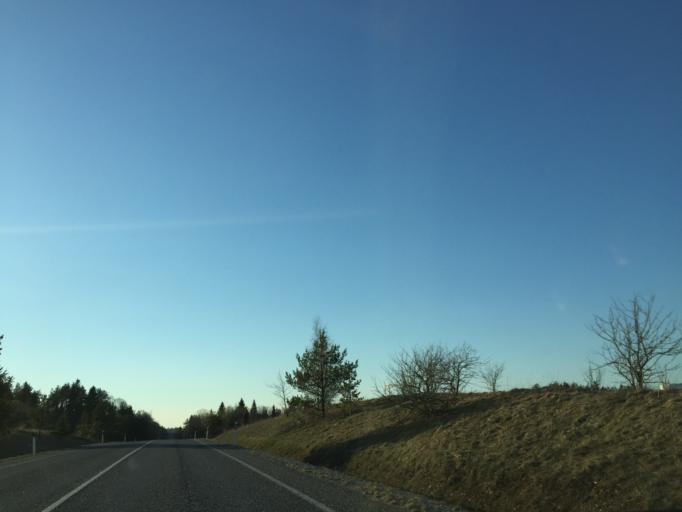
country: EE
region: Ida-Virumaa
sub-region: Johvi vald
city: Johvi
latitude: 59.1958
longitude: 27.5490
